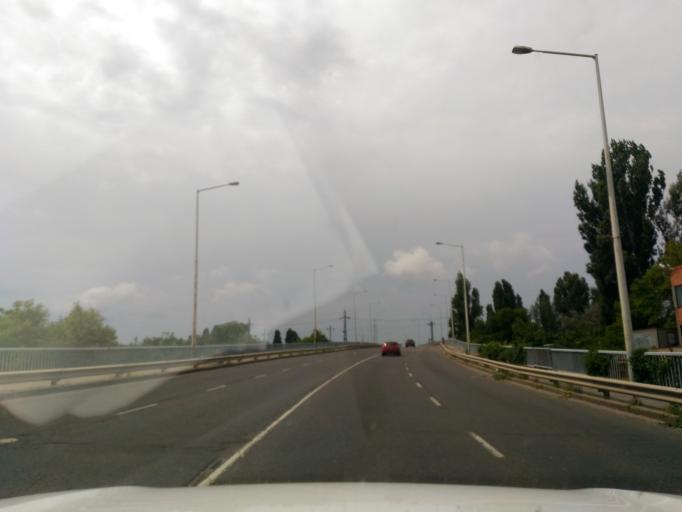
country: HU
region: Jasz-Nagykun-Szolnok
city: Szolnok
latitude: 47.1750
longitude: 20.1731
